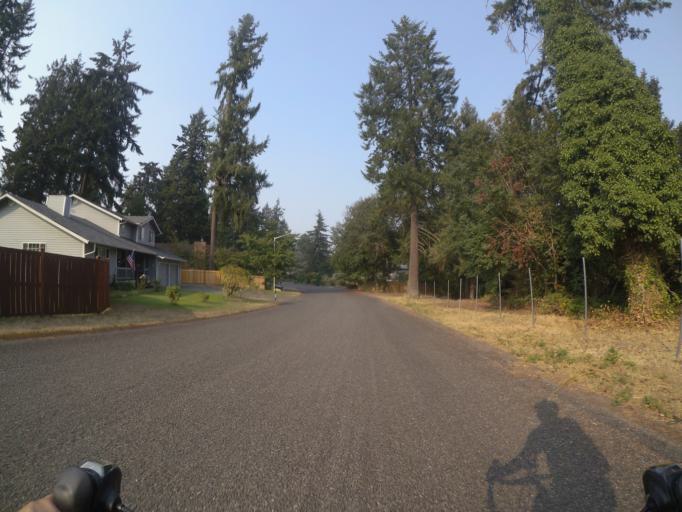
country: US
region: Washington
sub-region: Pierce County
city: Lakewood
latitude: 47.1427
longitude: -122.5209
